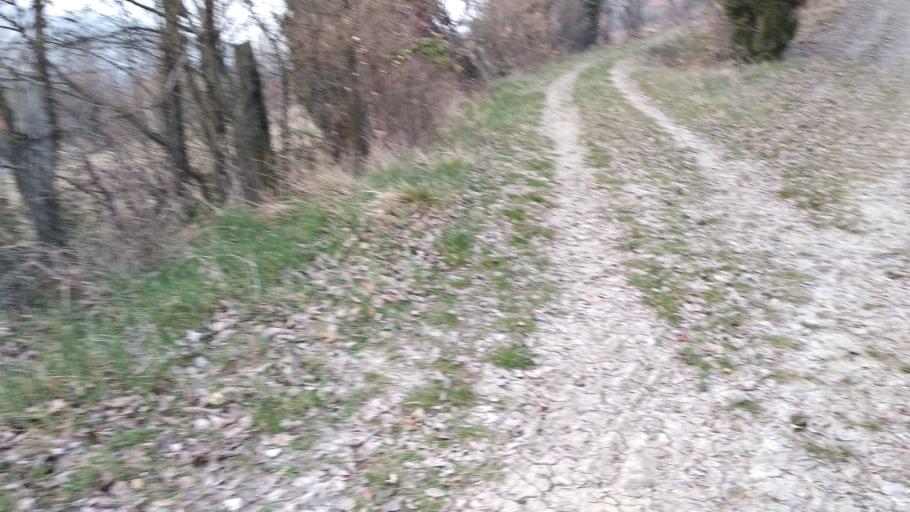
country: IT
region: Emilia-Romagna
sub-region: Provincia di Bologna
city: Pulce
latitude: 44.4145
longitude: 11.4309
